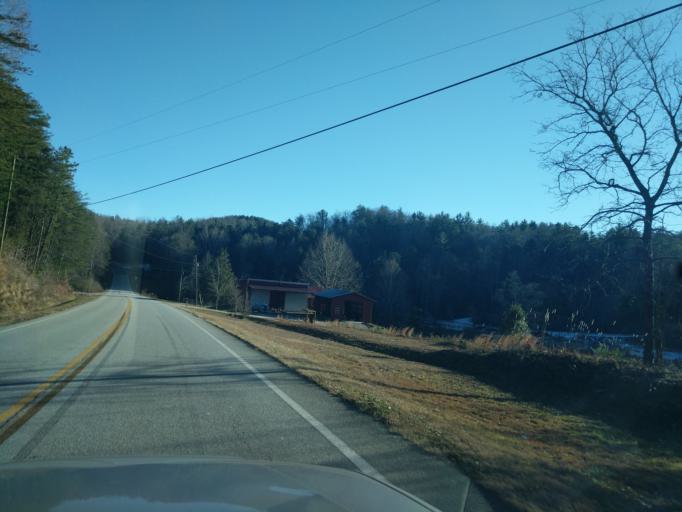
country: US
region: Georgia
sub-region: Rabun County
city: Clayton
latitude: 34.8386
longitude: -83.3331
